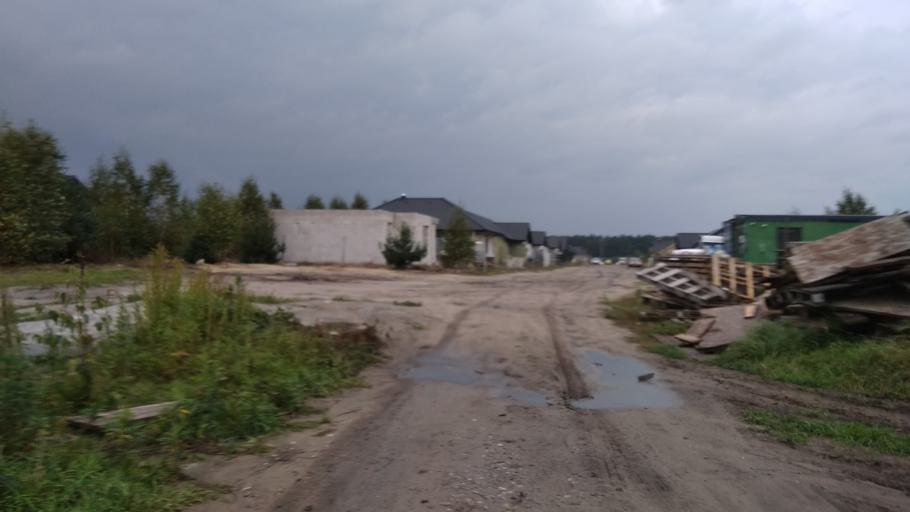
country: PL
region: Kujawsko-Pomorskie
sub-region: Powiat bydgoski
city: Osielsko
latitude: 53.2142
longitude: 18.1396
